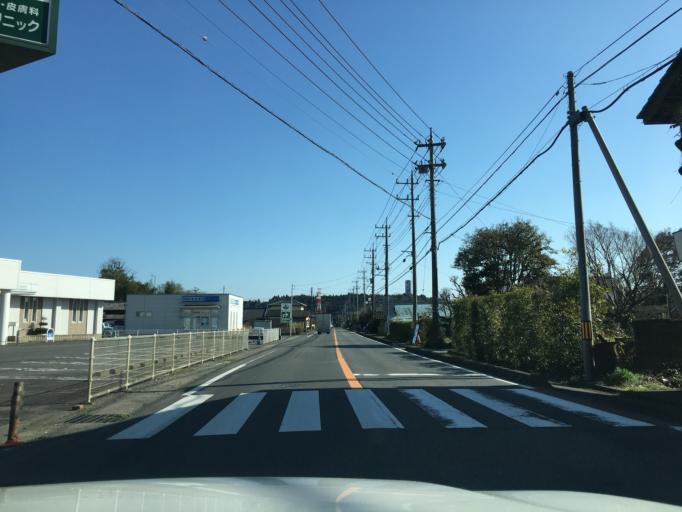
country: JP
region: Ibaraki
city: Omiya
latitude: 36.4953
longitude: 140.3731
